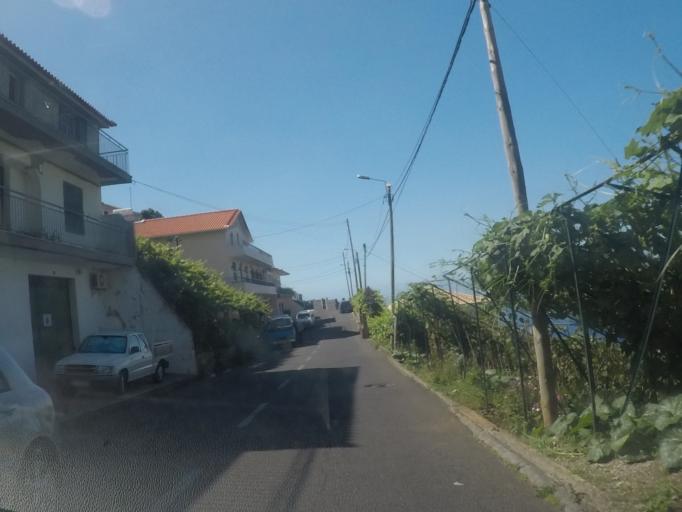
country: PT
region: Madeira
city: Camara de Lobos
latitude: 32.6725
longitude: -16.9709
